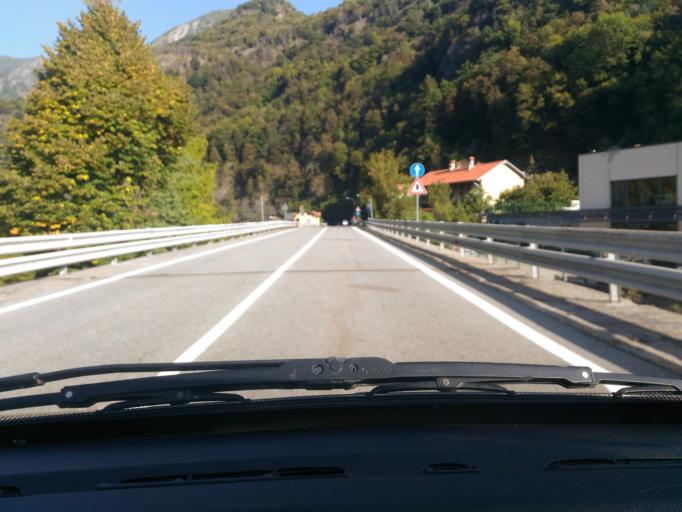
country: IT
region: Piedmont
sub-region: Provincia di Vercelli
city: Varallo
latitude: 45.8170
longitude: 8.2431
